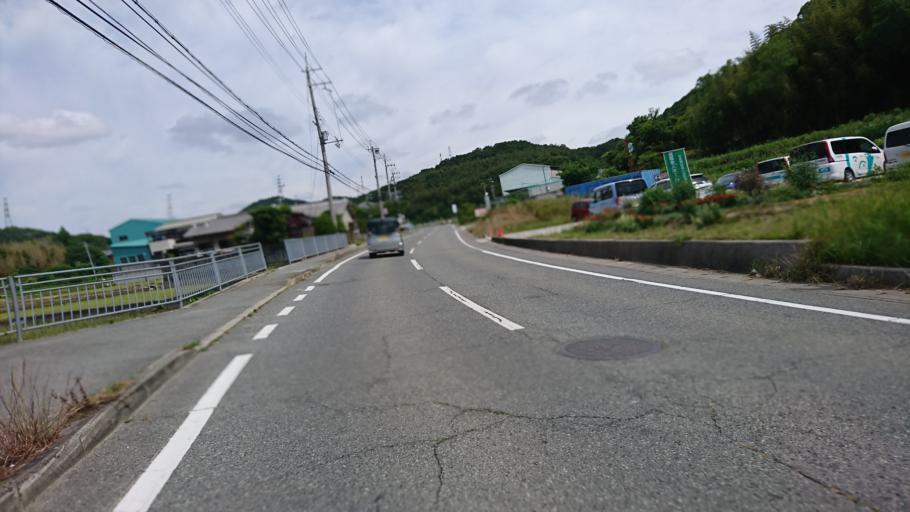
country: JP
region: Hyogo
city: Shirahamacho-usazakiminami
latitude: 34.7940
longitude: 134.7473
